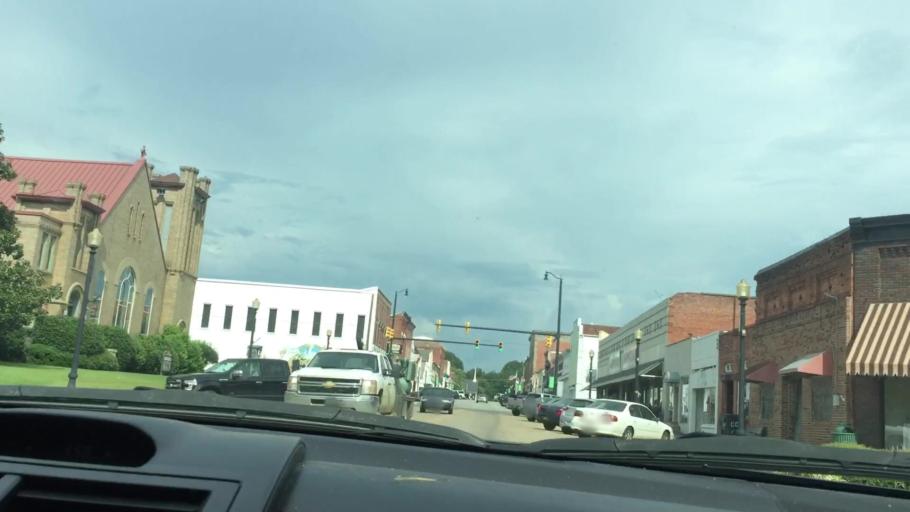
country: US
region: Alabama
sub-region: Hale County
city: Greensboro
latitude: 32.7041
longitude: -87.5964
